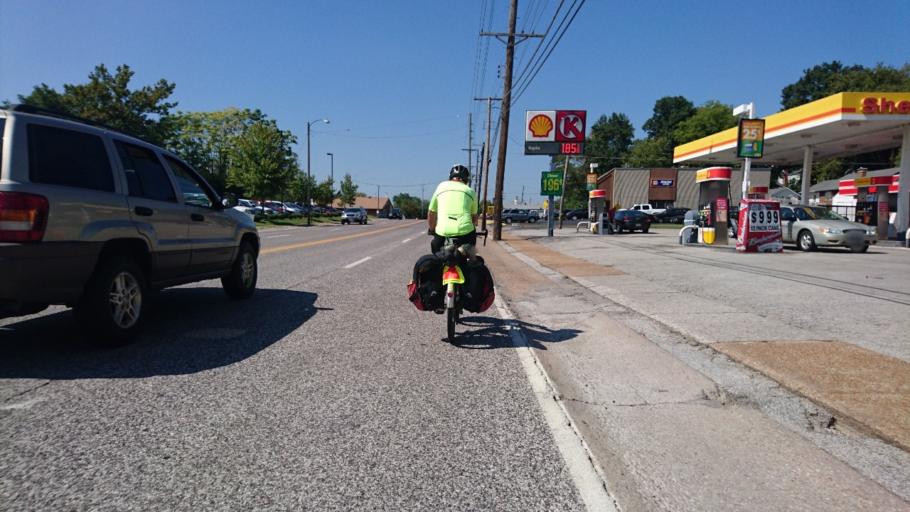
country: US
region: Missouri
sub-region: Saint Louis County
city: Brentwood
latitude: 38.6118
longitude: -90.3384
